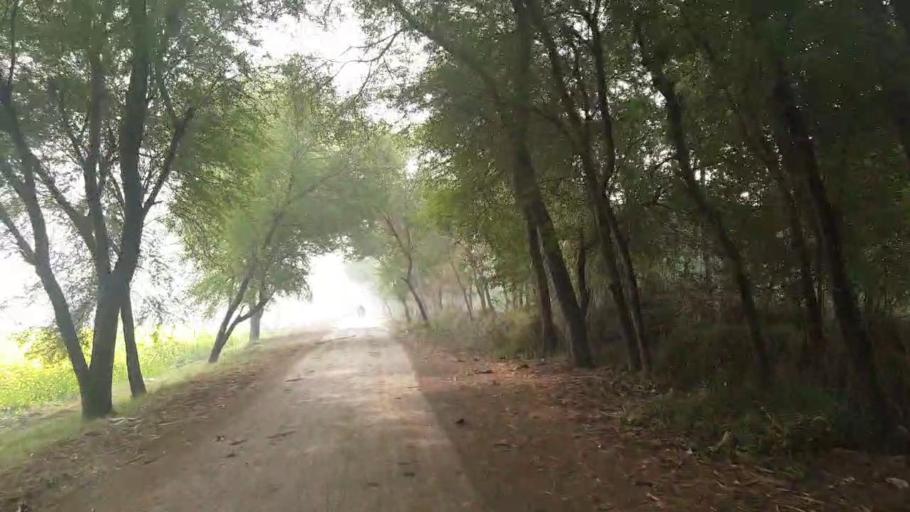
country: PK
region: Sindh
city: Tando Adam
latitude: 25.7917
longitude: 68.5962
